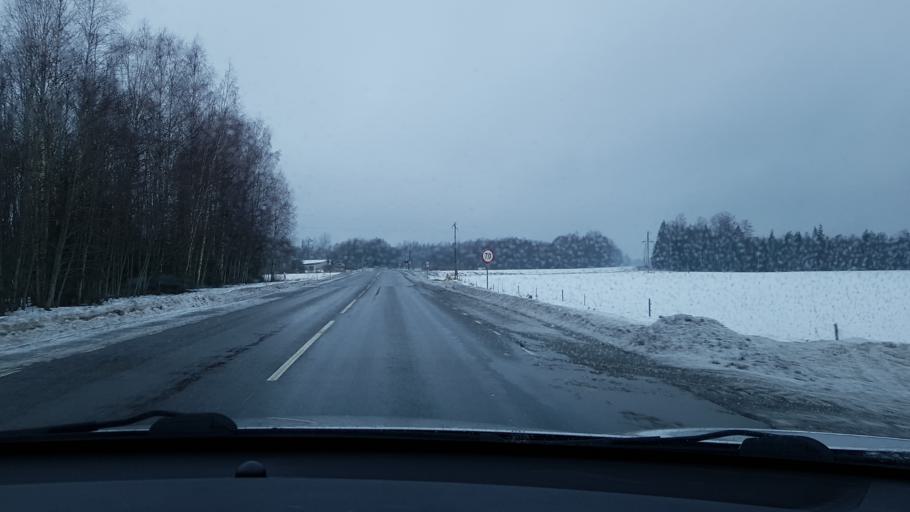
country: EE
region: Jaervamaa
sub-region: Tueri vald
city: Sarevere
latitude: 58.8129
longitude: 25.3556
